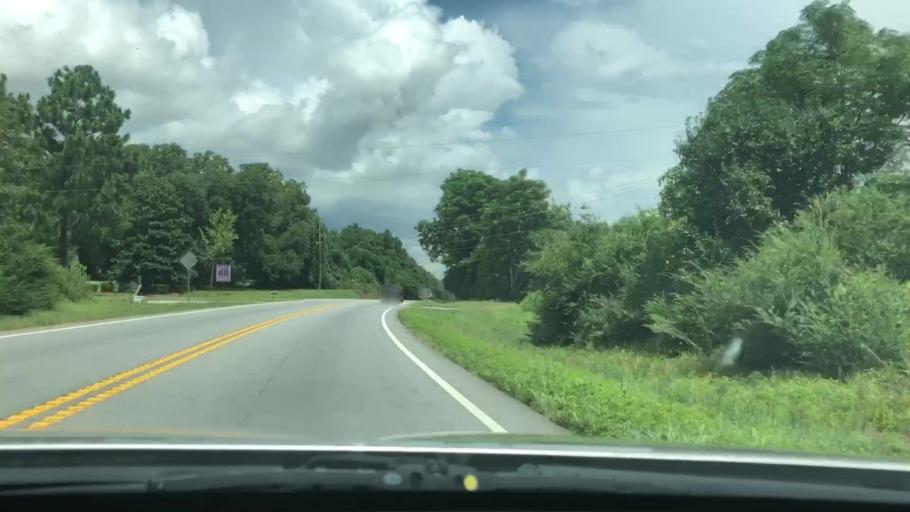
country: US
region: Georgia
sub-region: Lamar County
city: Barnesville
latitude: 33.1372
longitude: -84.1525
